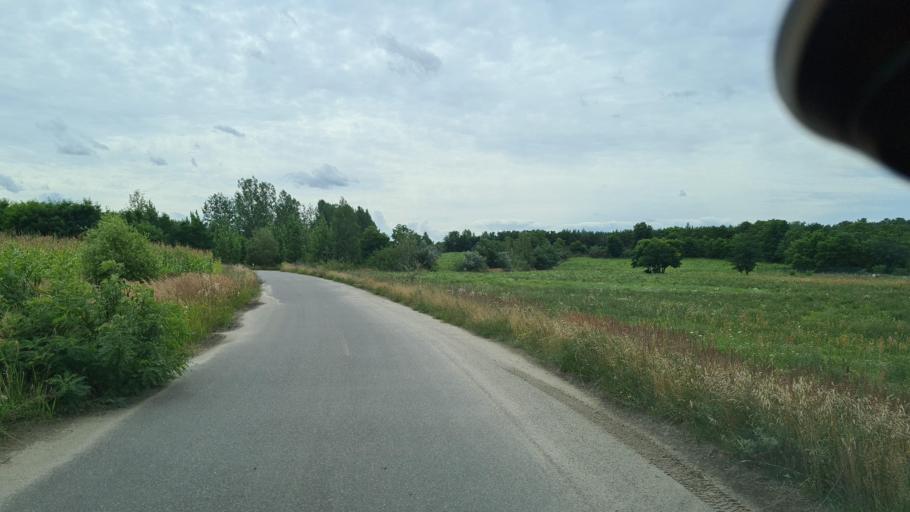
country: DE
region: Brandenburg
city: Spremberg
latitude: 51.5694
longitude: 14.2894
